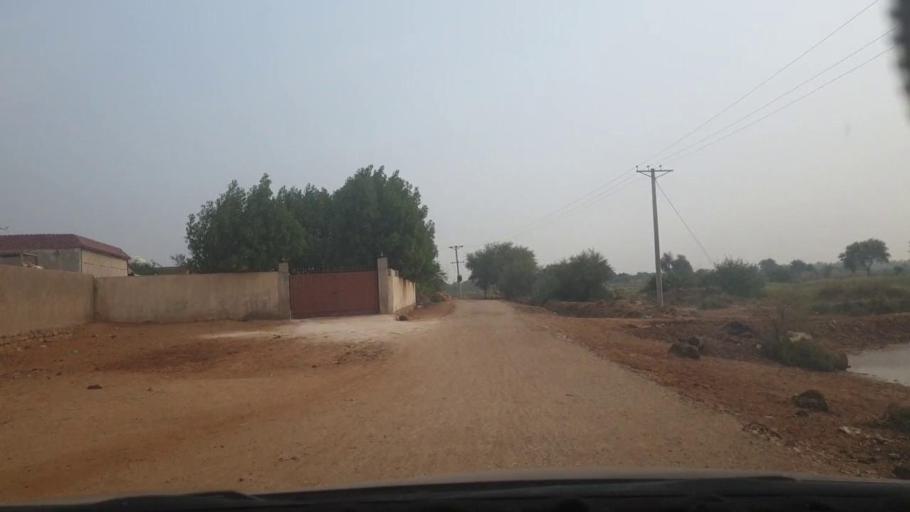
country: PK
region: Sindh
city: Jamshoro
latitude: 25.5145
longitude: 68.2937
